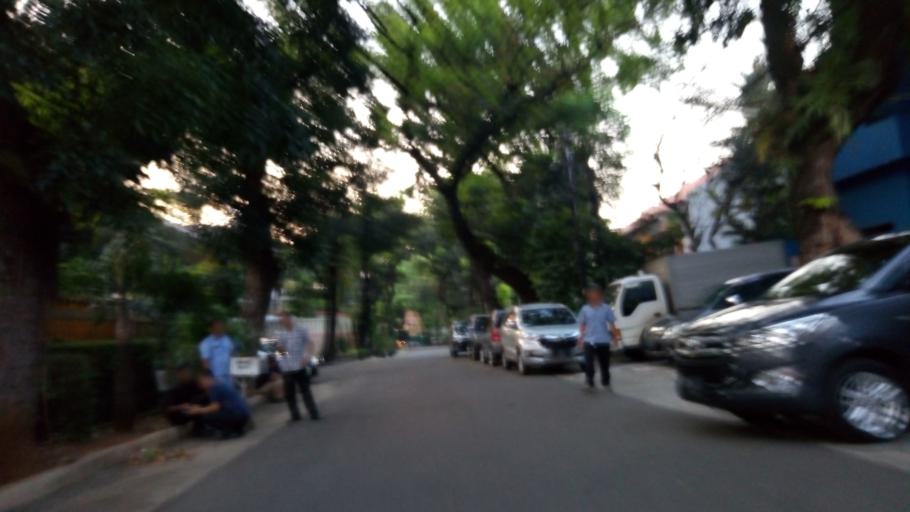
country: ID
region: Jakarta Raya
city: Jakarta
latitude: -6.2440
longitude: 106.7963
